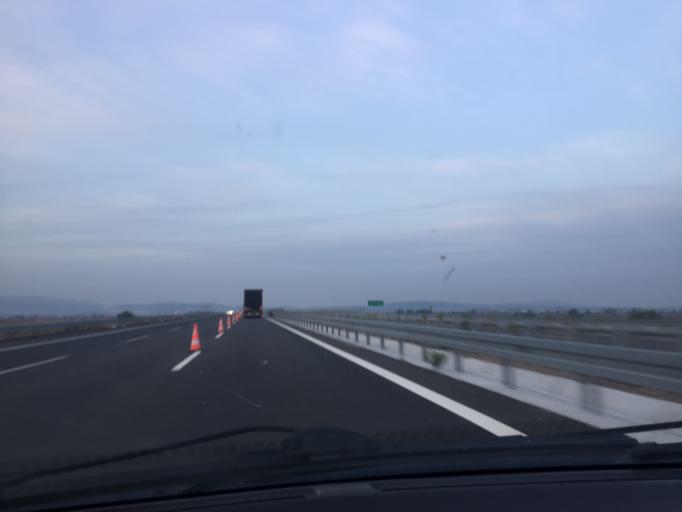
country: TR
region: Manisa
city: Halitpasa
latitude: 38.7337
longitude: 27.6564
